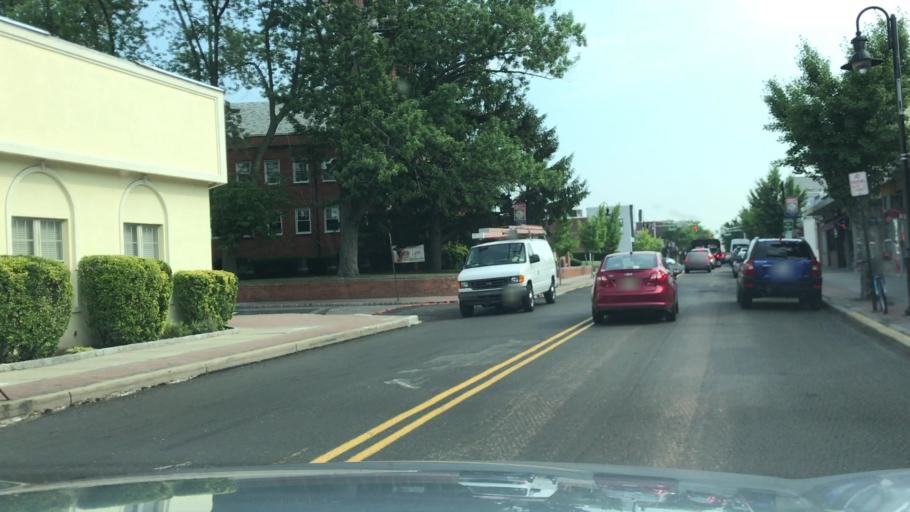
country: US
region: New Jersey
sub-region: Bergen County
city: Bergenfield
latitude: 40.9293
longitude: -73.9956
